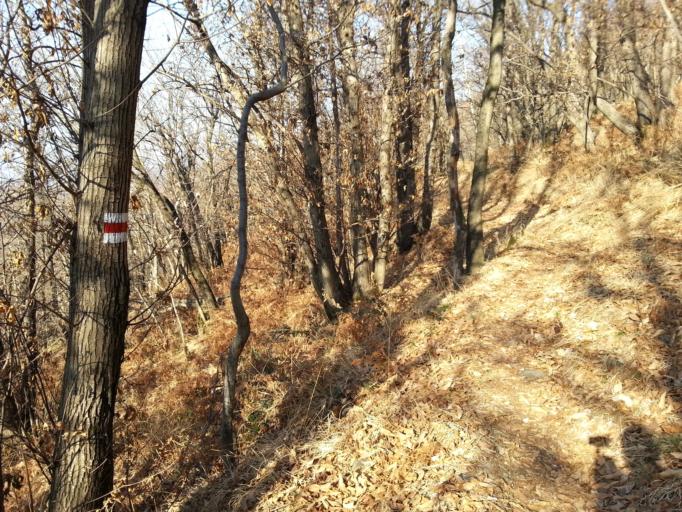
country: CH
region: Ticino
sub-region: Bellinzona District
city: Cadenazzo
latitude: 46.1303
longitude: 8.9251
